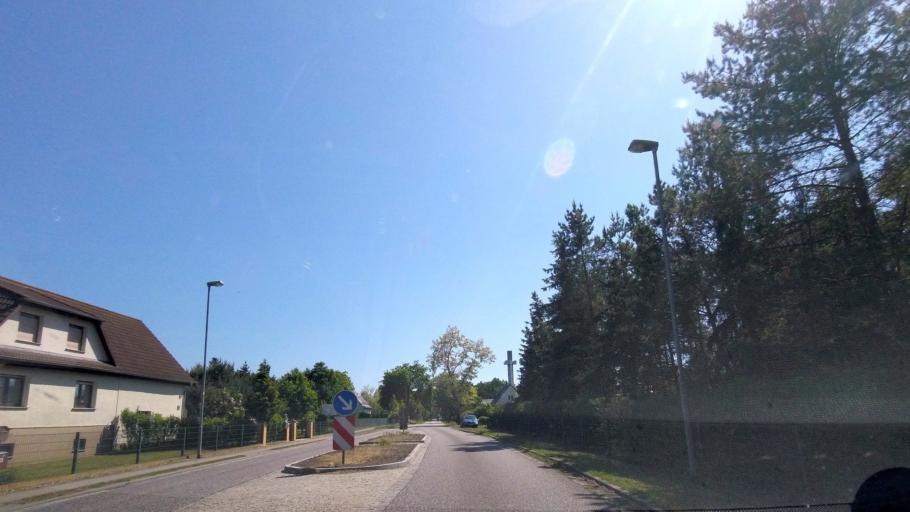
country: DE
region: Brandenburg
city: Gross Kreutz
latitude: 52.3526
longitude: 12.7652
